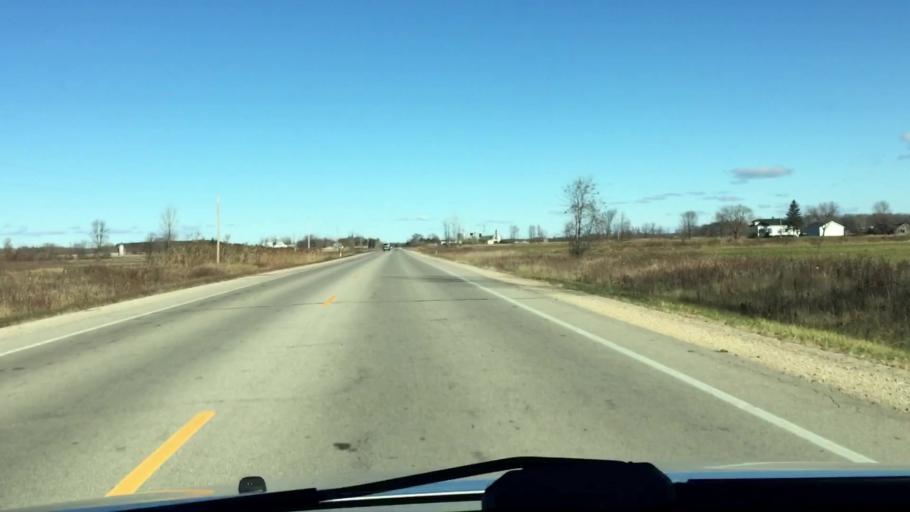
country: US
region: Wisconsin
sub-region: Brown County
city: Pulaski
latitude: 44.7196
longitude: -88.2458
